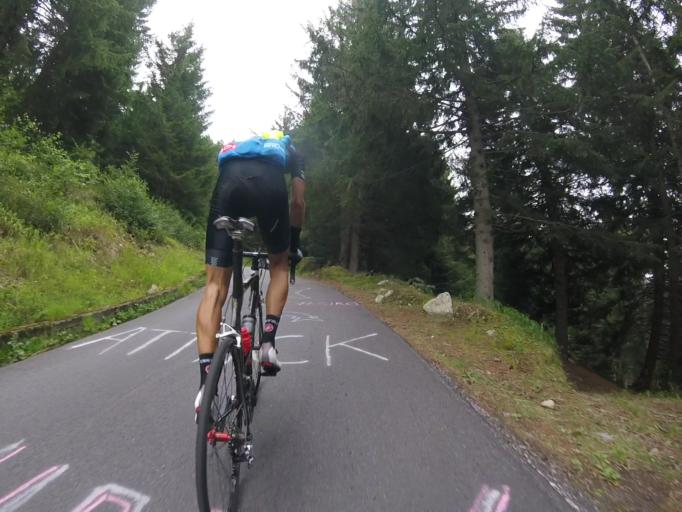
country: IT
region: Lombardy
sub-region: Provincia di Sondrio
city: Mazzo di Valtellina
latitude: 46.2527
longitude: 10.2886
